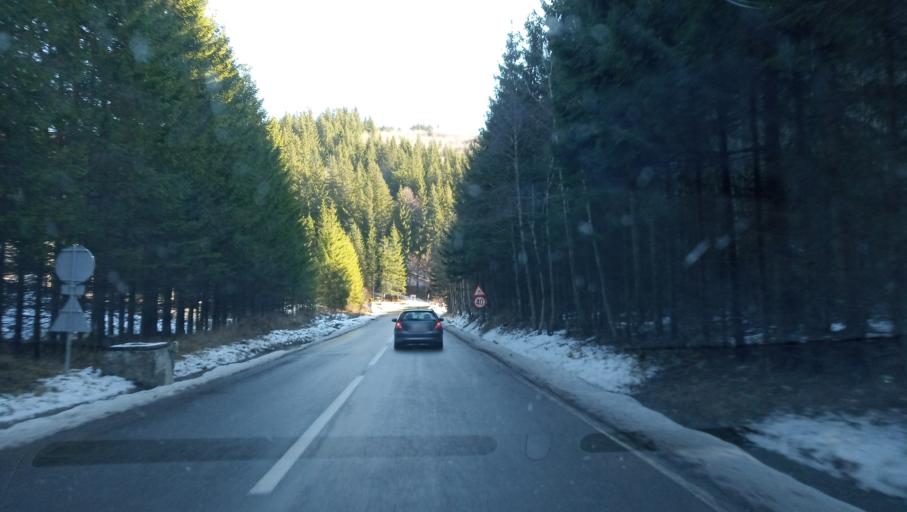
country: RO
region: Brasov
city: Crivina
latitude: 45.4828
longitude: 25.9183
